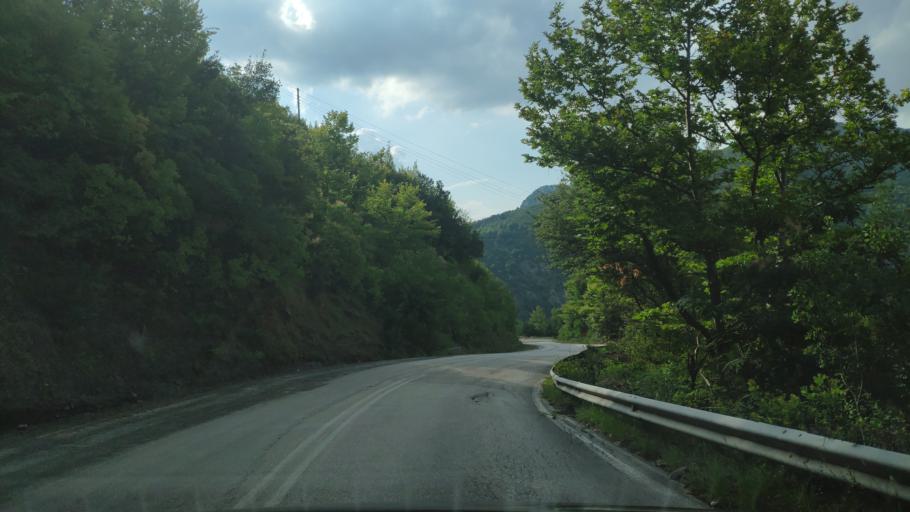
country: GR
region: Epirus
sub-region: Nomos Artas
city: Agios Dimitrios
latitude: 39.4589
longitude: 21.0399
